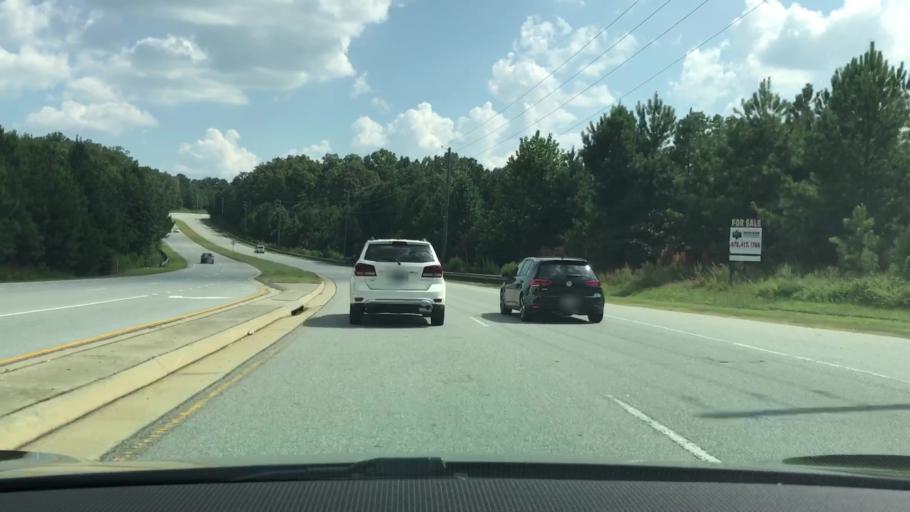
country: US
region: Georgia
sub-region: Gwinnett County
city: Sugar Hill
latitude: 34.0694
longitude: -84.0192
